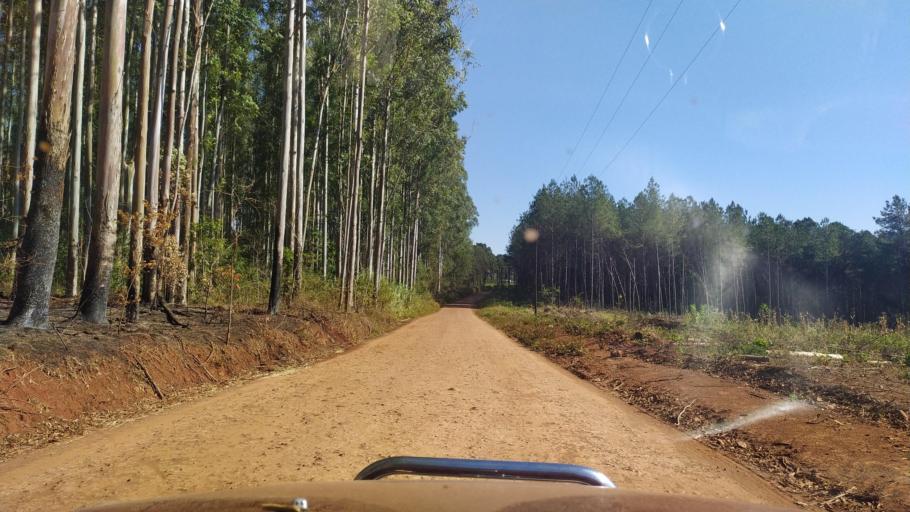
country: AR
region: Misiones
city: El Alcazar
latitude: -26.7153
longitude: -54.7068
